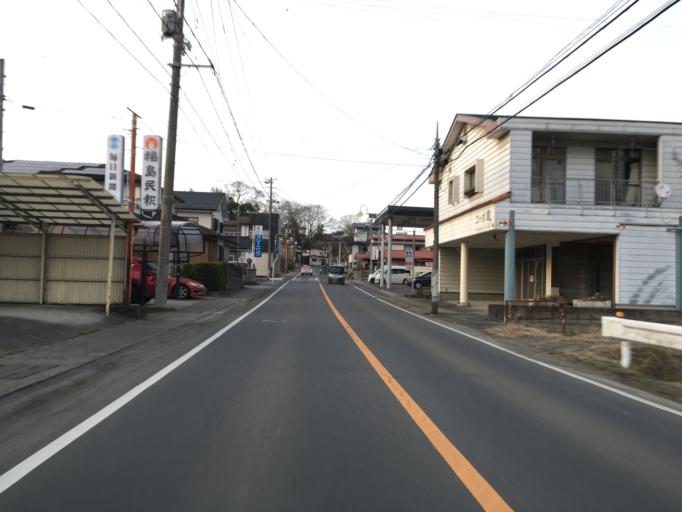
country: JP
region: Fukushima
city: Ishikawa
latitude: 37.0206
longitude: 140.3912
